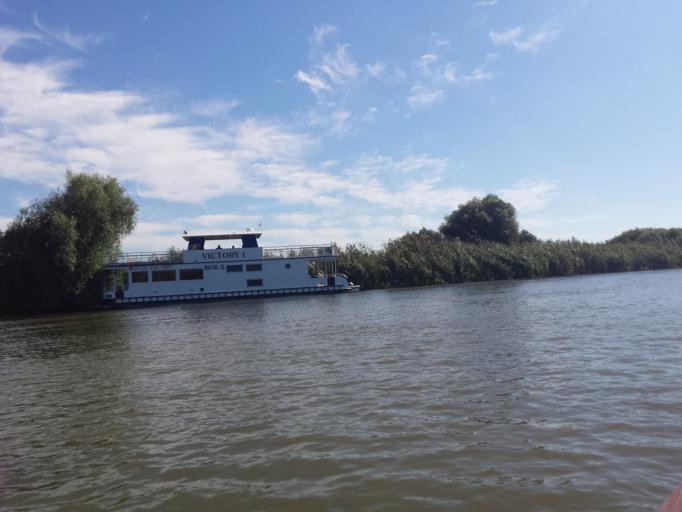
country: RO
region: Tulcea
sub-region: Comuna Mahmudia
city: Mahmudia
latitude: 45.2383
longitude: 29.1379
